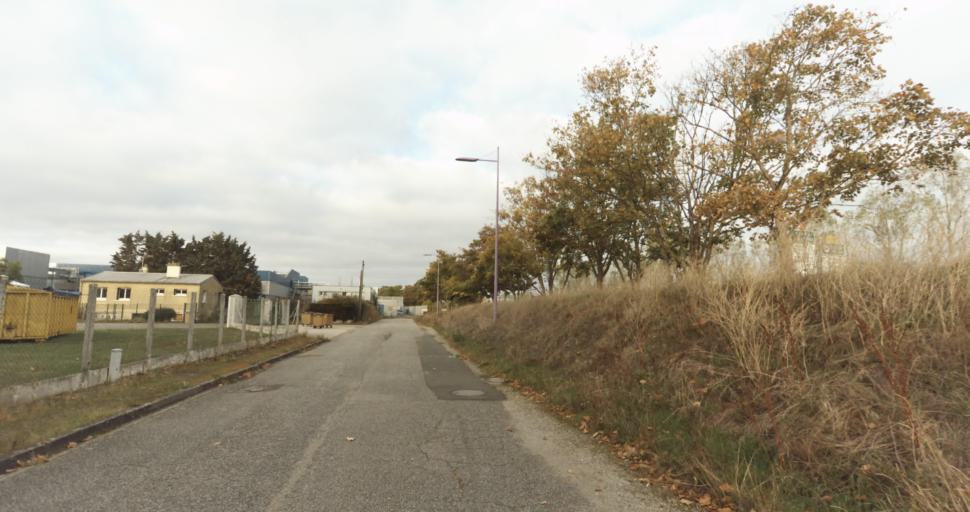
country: FR
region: Centre
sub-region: Departement d'Eure-et-Loir
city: Vernouillet
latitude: 48.7156
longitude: 1.3725
